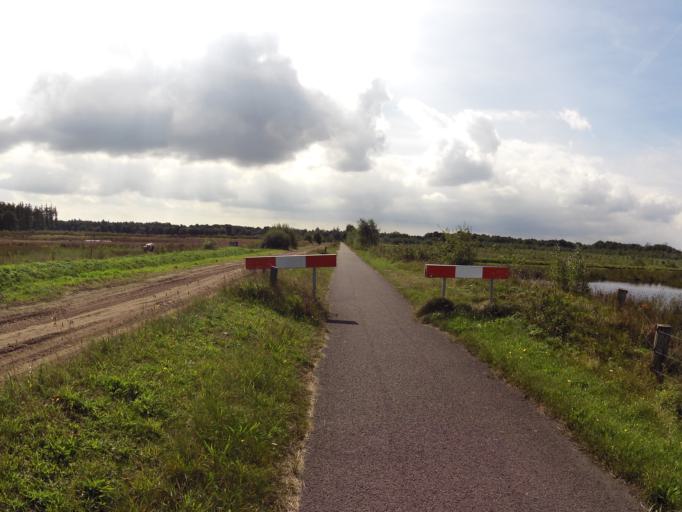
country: NL
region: Drenthe
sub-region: Gemeente Hoogeveen
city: Hoogeveen
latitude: 52.7661
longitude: 6.5733
